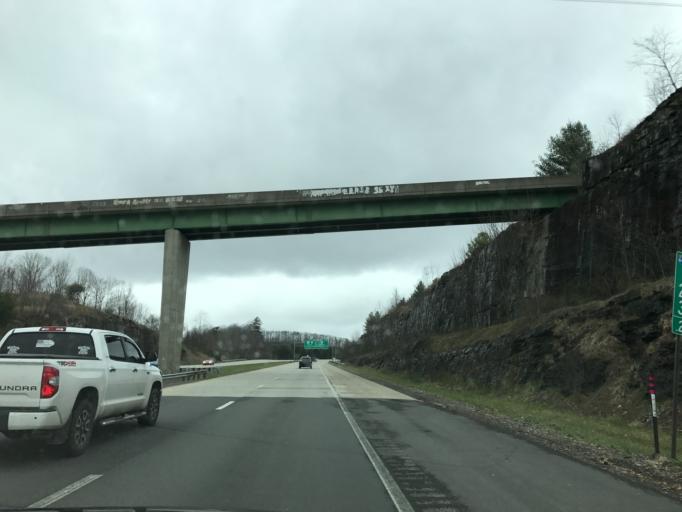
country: US
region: West Virginia
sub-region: Raleigh County
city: Beaver
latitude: 37.7568
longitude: -81.1501
